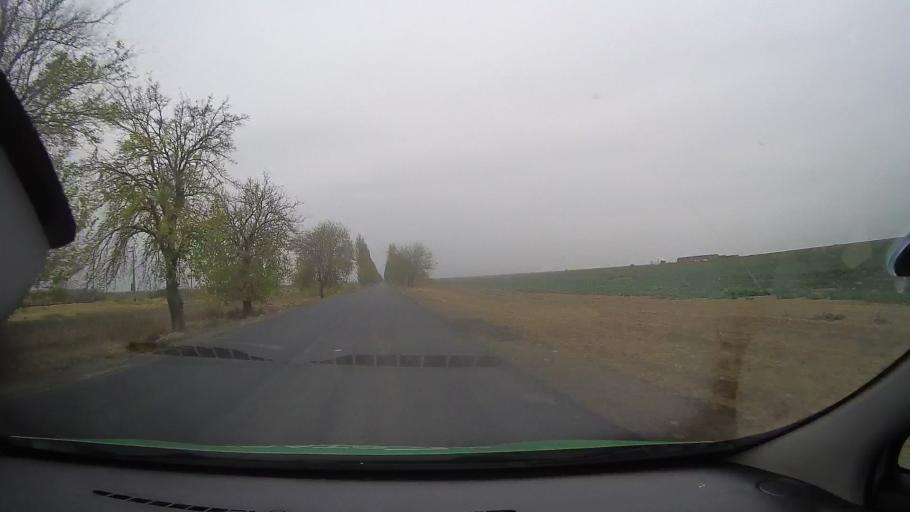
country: RO
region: Ialomita
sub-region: Comuna Valea Ciorii
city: Valea Ciorii
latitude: 44.7076
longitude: 27.5939
